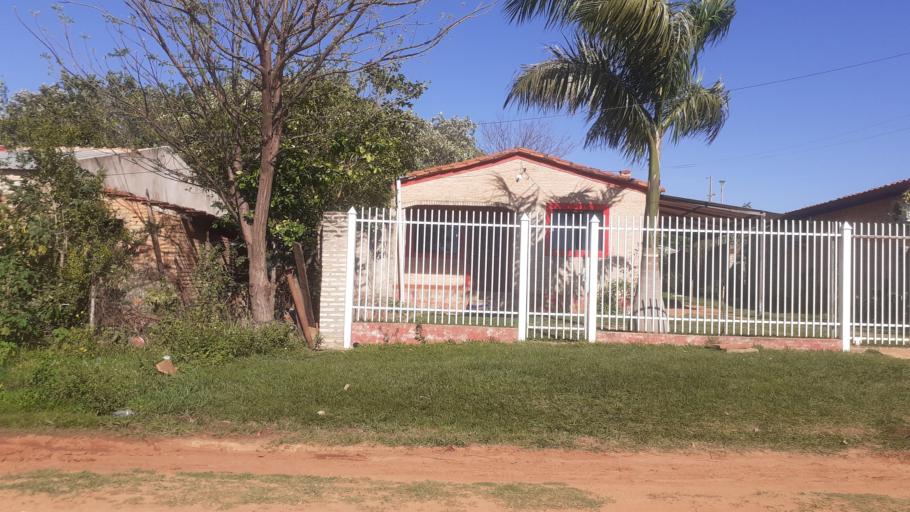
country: PY
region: Misiones
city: San Juan Bautista
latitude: -26.6665
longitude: -57.1237
